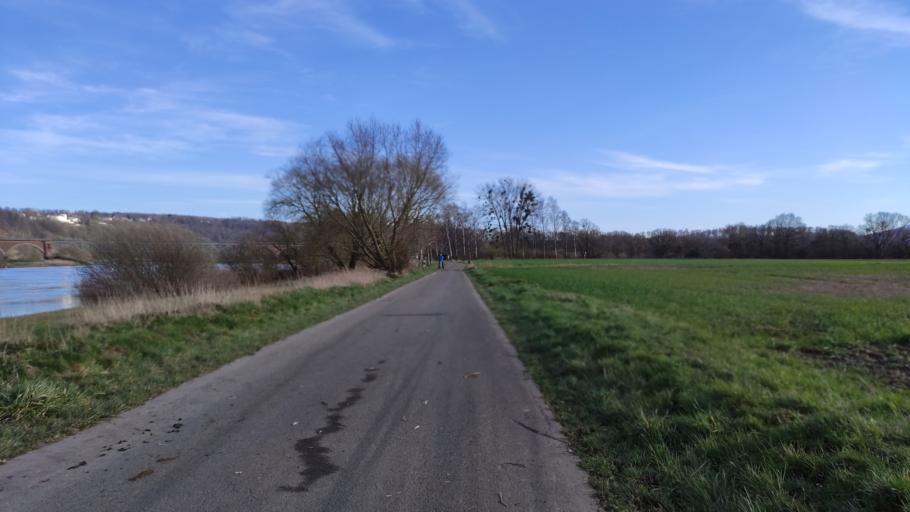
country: DE
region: Lower Saxony
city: Boffzen
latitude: 51.7393
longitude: 9.3760
